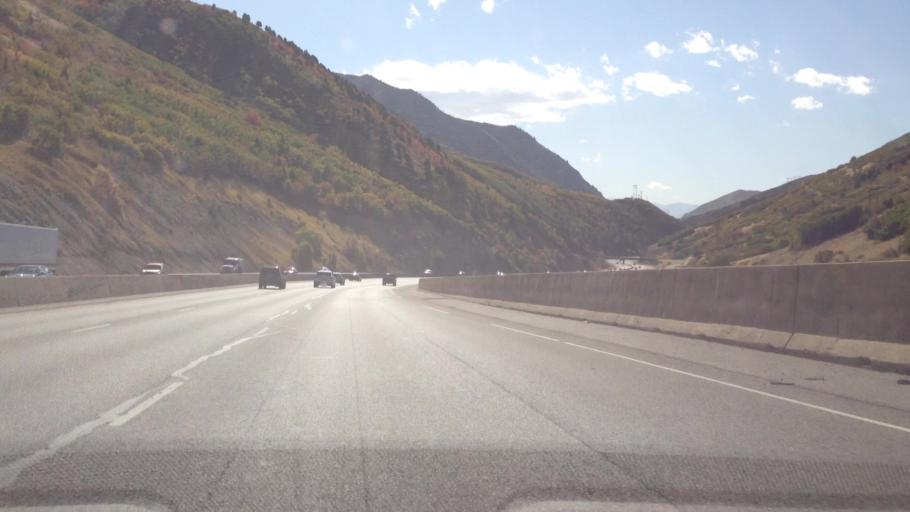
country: US
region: Utah
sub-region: Salt Lake County
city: Mount Olympus
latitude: 40.7500
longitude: -111.7202
